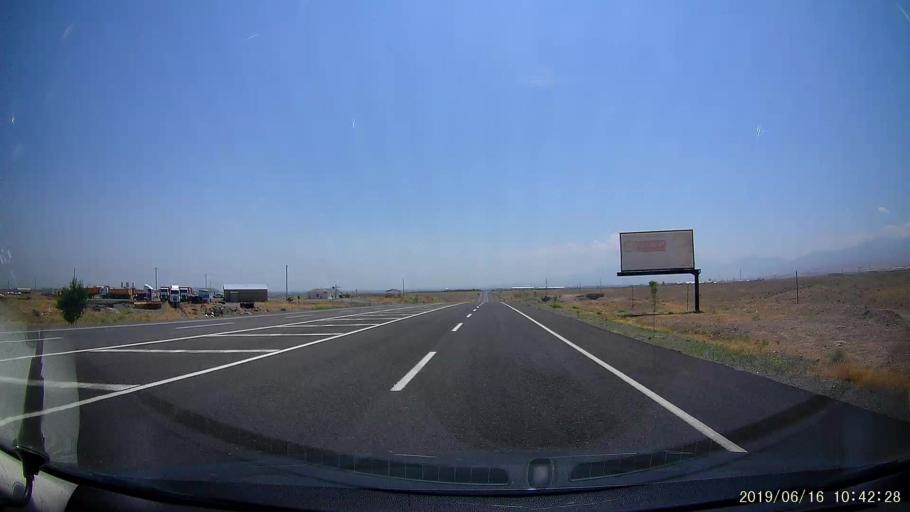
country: AM
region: Armavir
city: Shenavan
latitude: 40.0417
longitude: 43.8074
